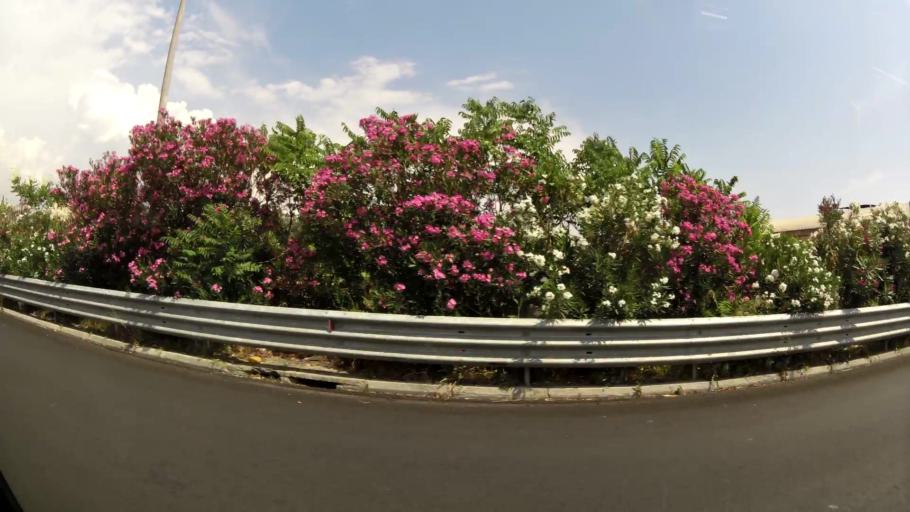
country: GR
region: Central Macedonia
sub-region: Nomos Thessalonikis
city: Menemeni
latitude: 40.6720
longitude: 22.8877
